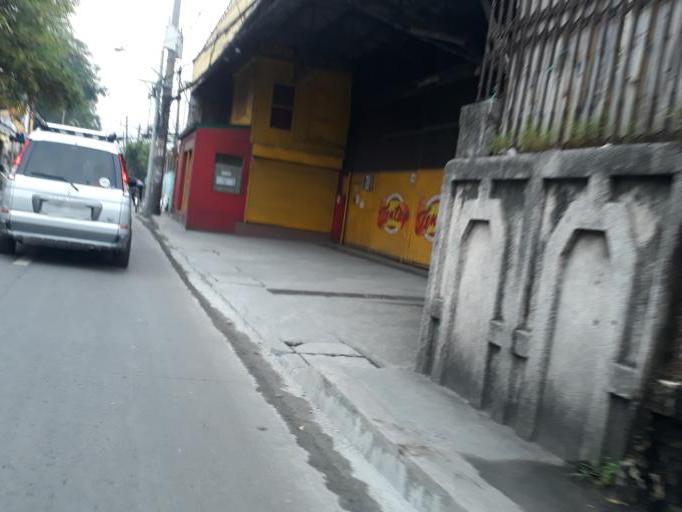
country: PH
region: Calabarzon
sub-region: Province of Rizal
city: Navotas
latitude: 14.6625
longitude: 120.9433
